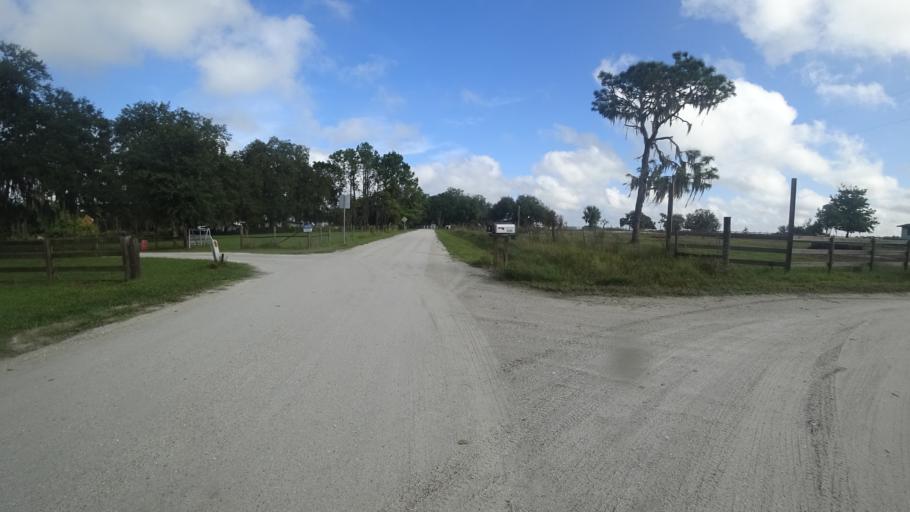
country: US
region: Florida
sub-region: Hillsborough County
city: Wimauma
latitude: 27.4753
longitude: -82.2560
